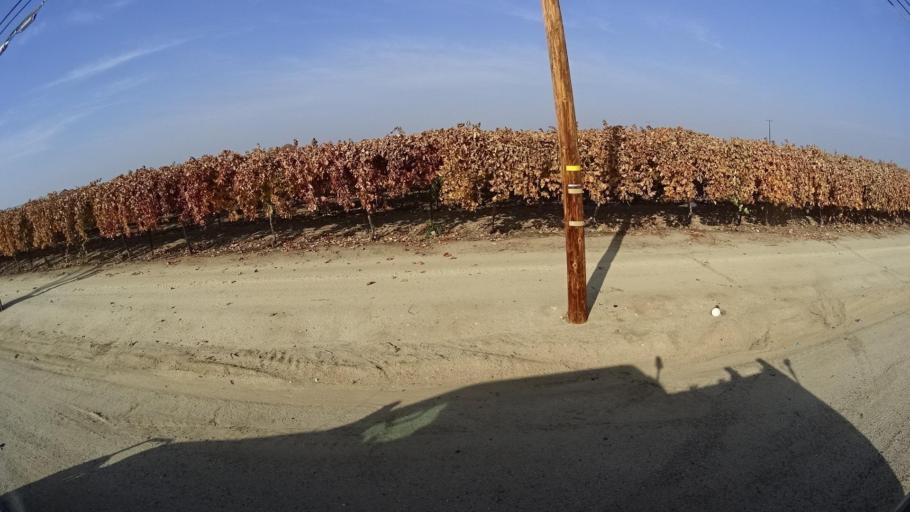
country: US
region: California
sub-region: Kern County
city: Delano
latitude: 35.7760
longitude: -119.1843
